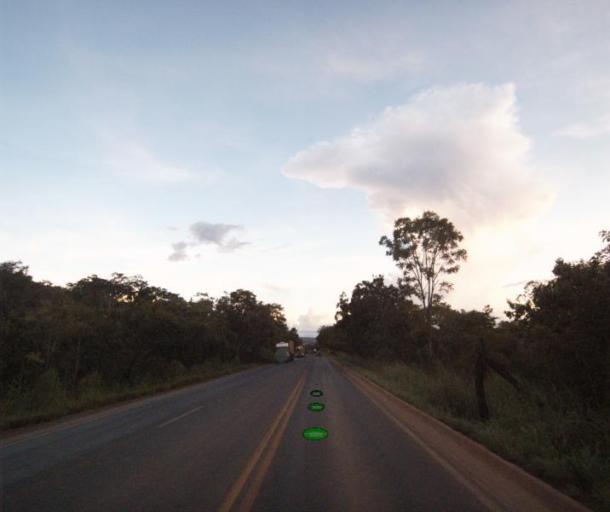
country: BR
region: Goias
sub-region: Uruacu
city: Uruacu
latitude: -14.4862
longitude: -49.1535
